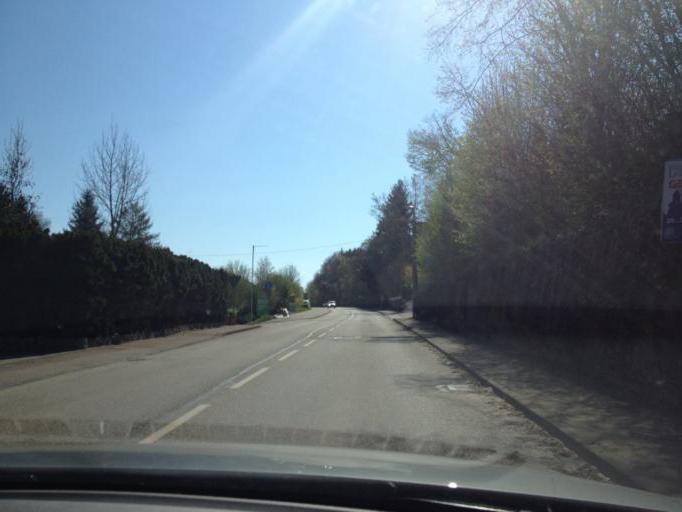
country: DE
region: Baden-Wuerttemberg
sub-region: Regierungsbezirk Stuttgart
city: Neuenstadt am Kocher
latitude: 49.2322
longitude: 9.3352
